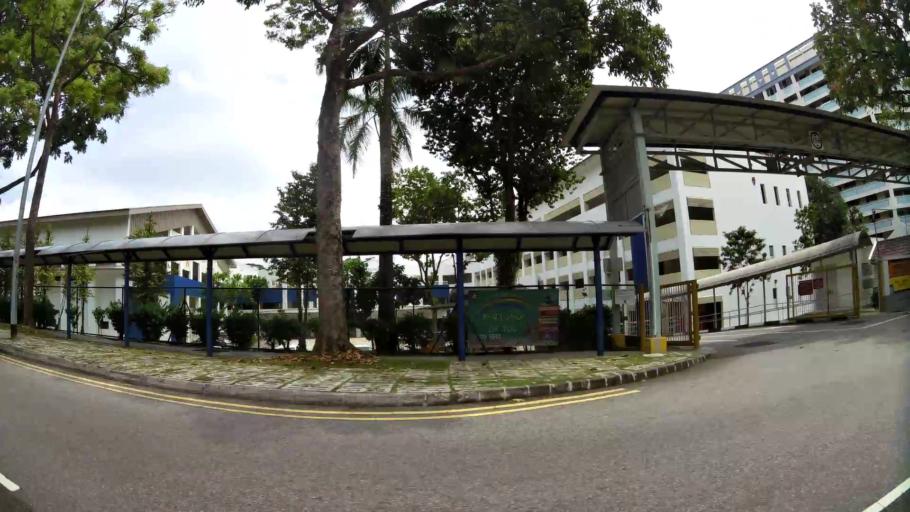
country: MY
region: Johor
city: Johor Bahru
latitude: 1.3820
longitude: 103.7729
